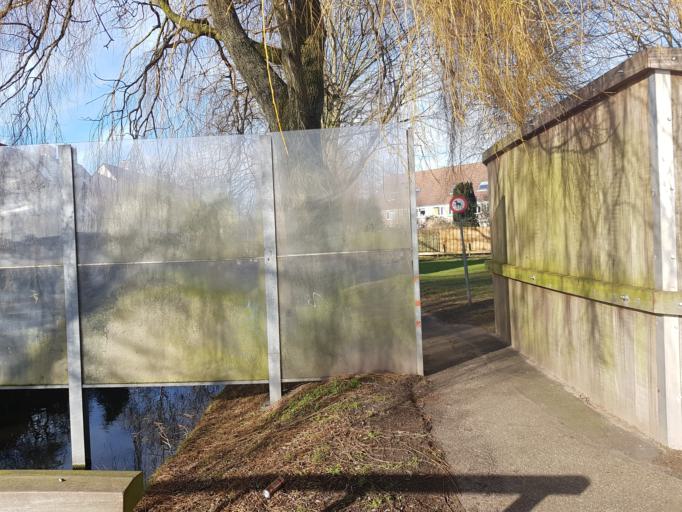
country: NL
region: North Holland
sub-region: Gemeente Bloemendaal
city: Bennebroek
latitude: 52.3185
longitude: 4.5796
